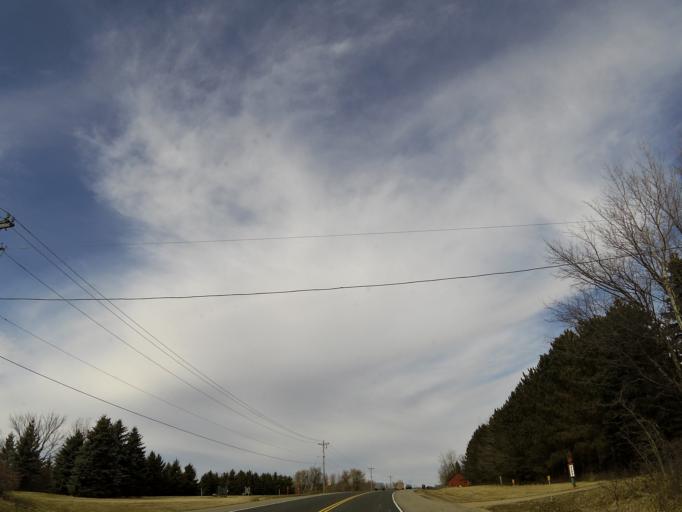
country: US
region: Minnesota
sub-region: Washington County
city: Lake Elmo
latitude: 44.9851
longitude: -92.8628
